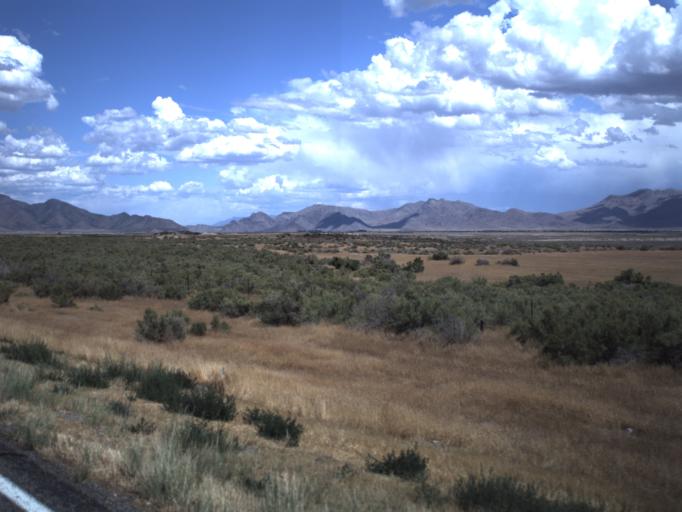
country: US
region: Utah
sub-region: Millard County
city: Delta
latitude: 39.5019
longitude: -112.3905
